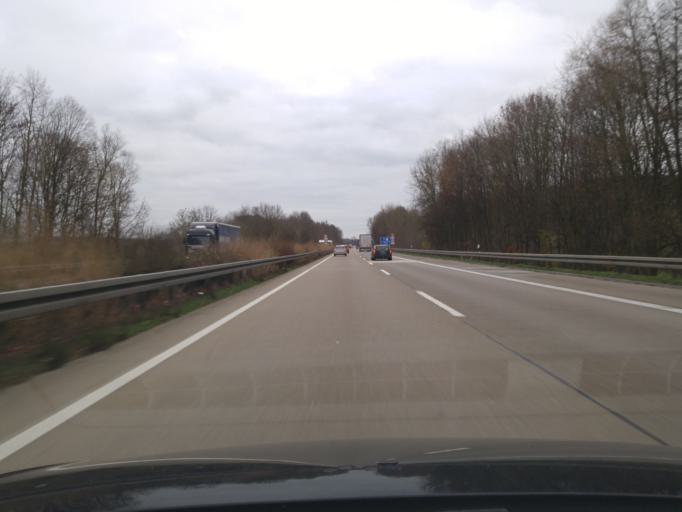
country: DE
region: Lower Saxony
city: Seesen
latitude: 51.8658
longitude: 10.1263
